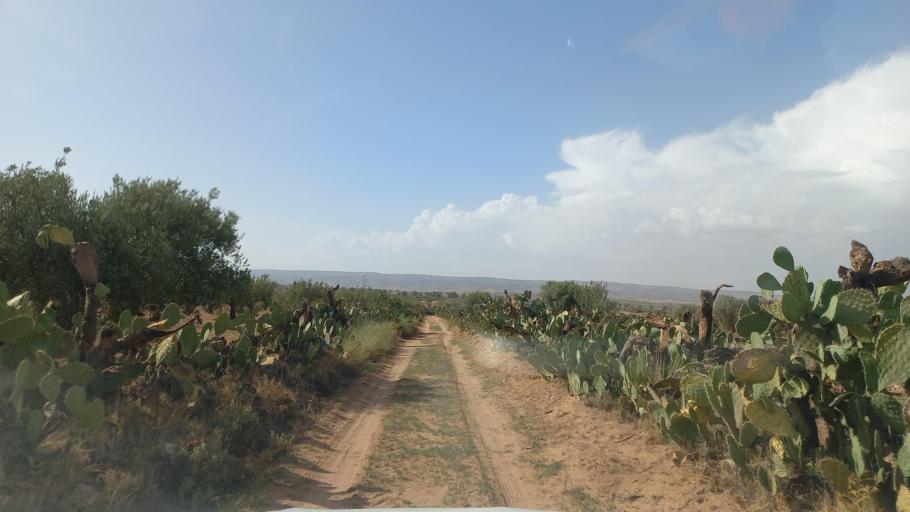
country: TN
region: Al Qasrayn
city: Kasserine
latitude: 35.2155
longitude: 8.9492
